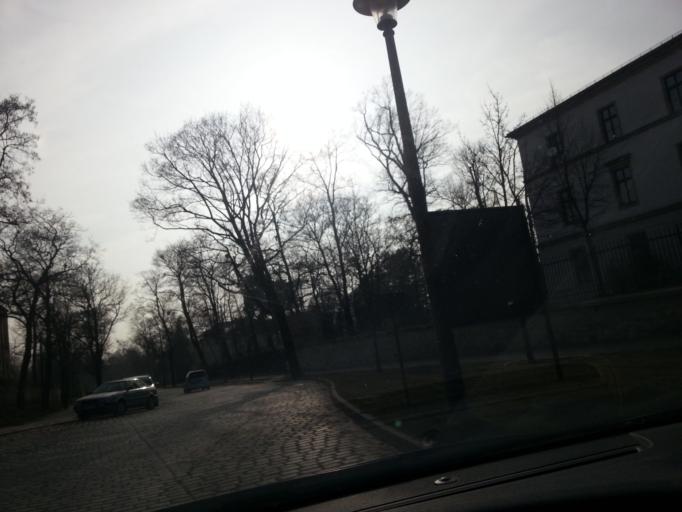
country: DE
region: Saxony
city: Albertstadt
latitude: 51.0751
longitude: 13.7673
